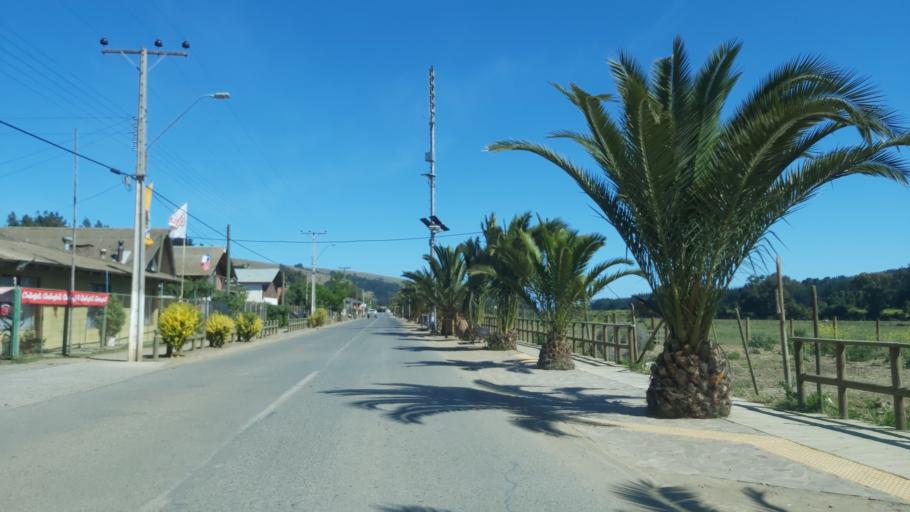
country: CL
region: Maule
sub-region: Provincia de Talca
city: Constitucion
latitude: -34.7687
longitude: -72.0710
